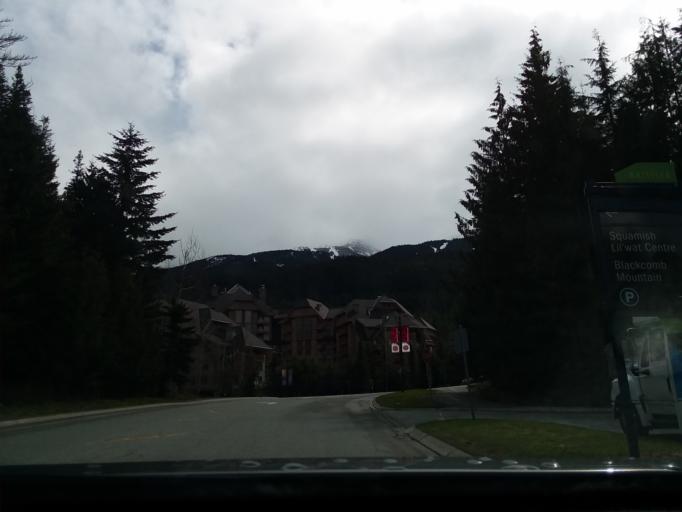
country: CA
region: British Columbia
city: Whistler
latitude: 50.1190
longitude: -122.9468
